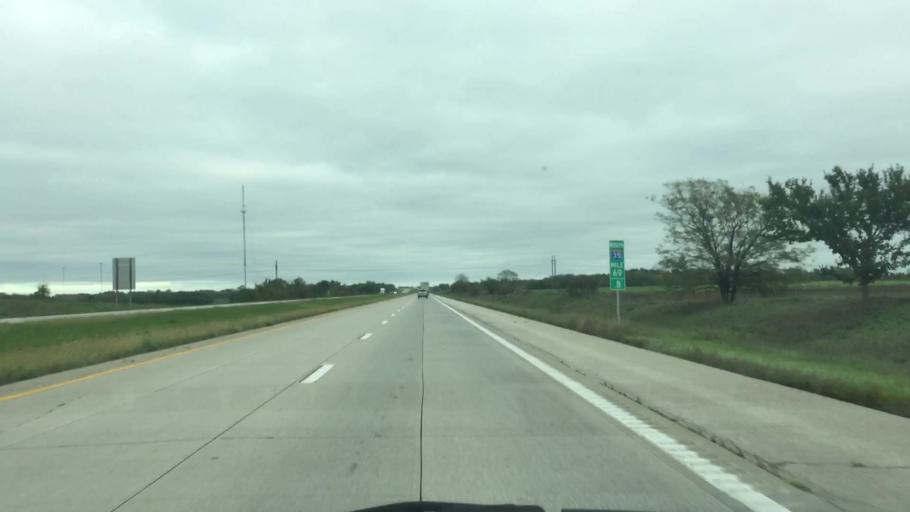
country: US
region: Missouri
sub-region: Daviess County
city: Gallatin
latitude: 39.9589
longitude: -94.1042
